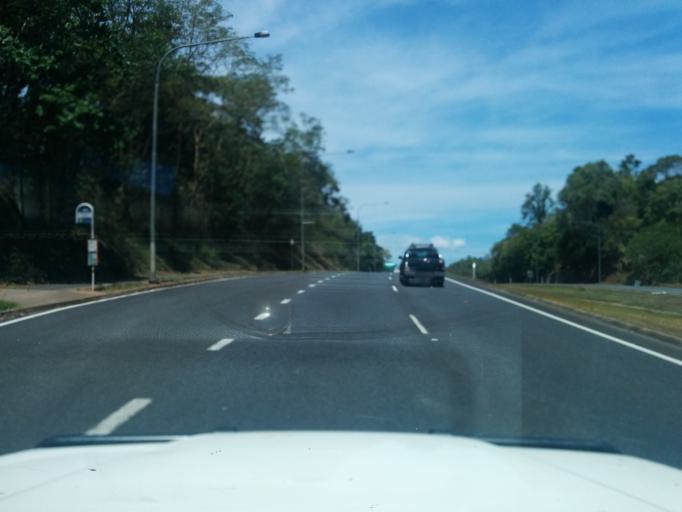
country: AU
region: Queensland
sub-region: Cairns
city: Redlynch
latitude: -16.9133
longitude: 145.7223
